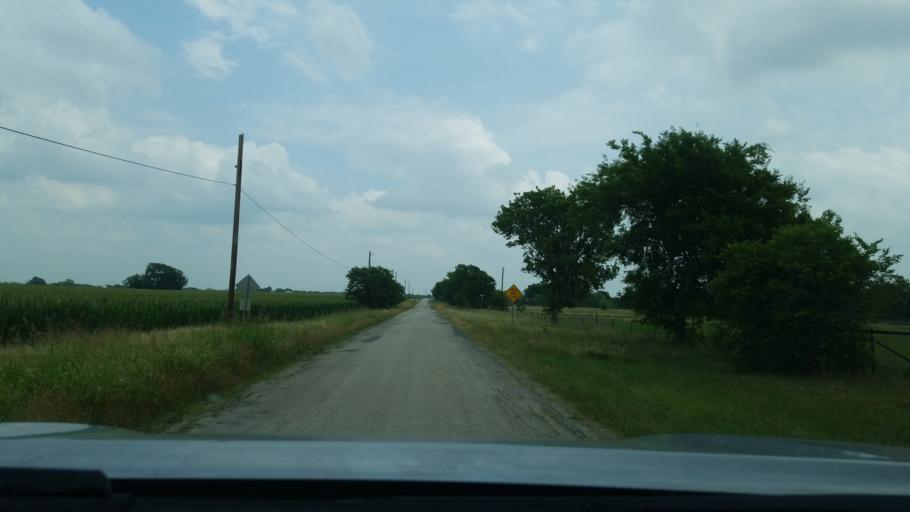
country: US
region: Texas
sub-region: Guadalupe County
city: Geronimo
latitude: 29.6801
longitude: -98.0134
